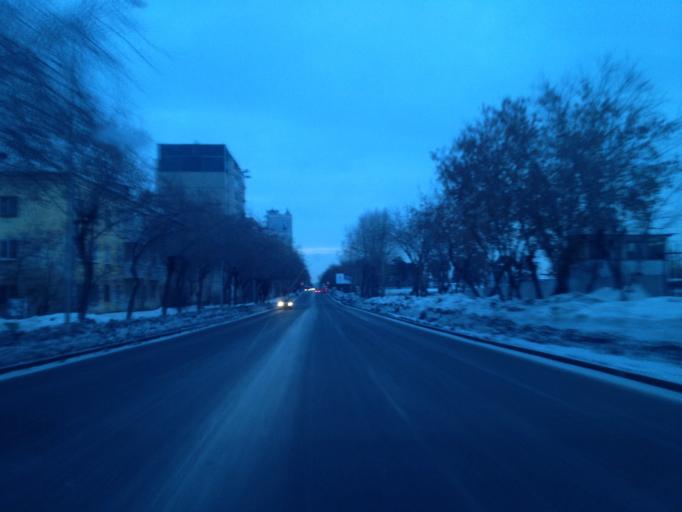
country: RU
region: Sverdlovsk
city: Sovkhoznyy
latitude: 56.7589
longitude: 60.6110
